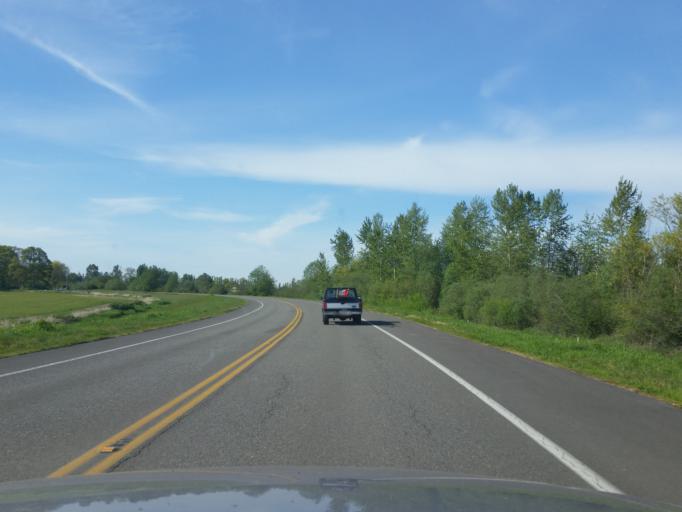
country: US
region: Washington
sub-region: Snohomish County
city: Everett
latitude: 47.9382
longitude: -122.1714
